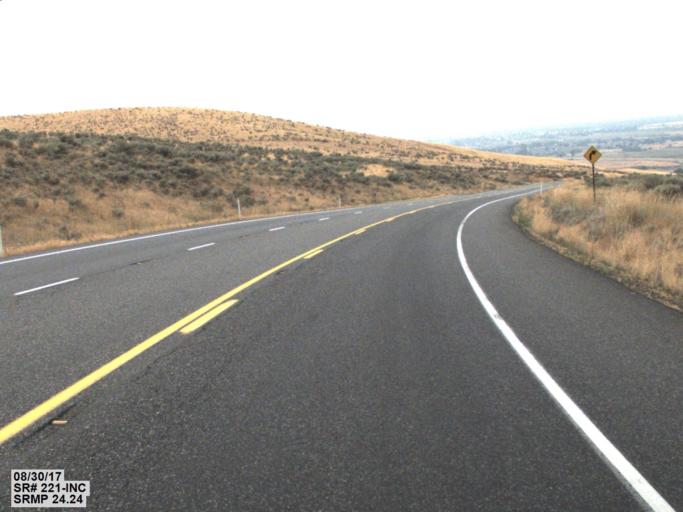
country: US
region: Washington
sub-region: Benton County
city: Prosser
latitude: 46.1996
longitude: -119.7183
